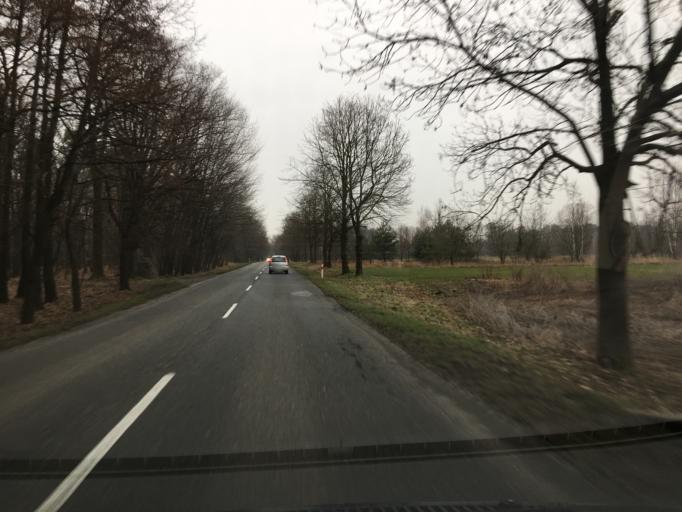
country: PL
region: Opole Voivodeship
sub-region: Powiat kedzierzynsko-kozielski
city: Bierawa
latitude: 50.3026
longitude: 18.2307
